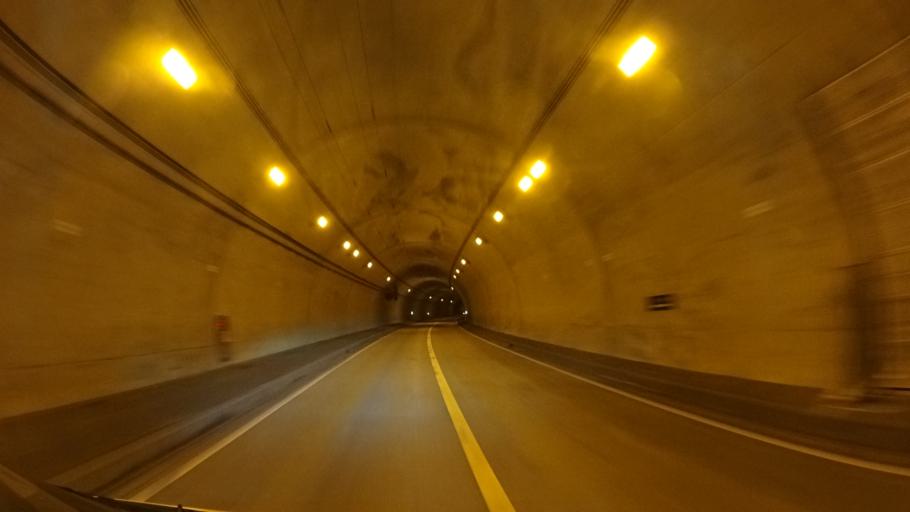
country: JP
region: Kyoto
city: Fukuchiyama
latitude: 35.4156
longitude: 135.0391
